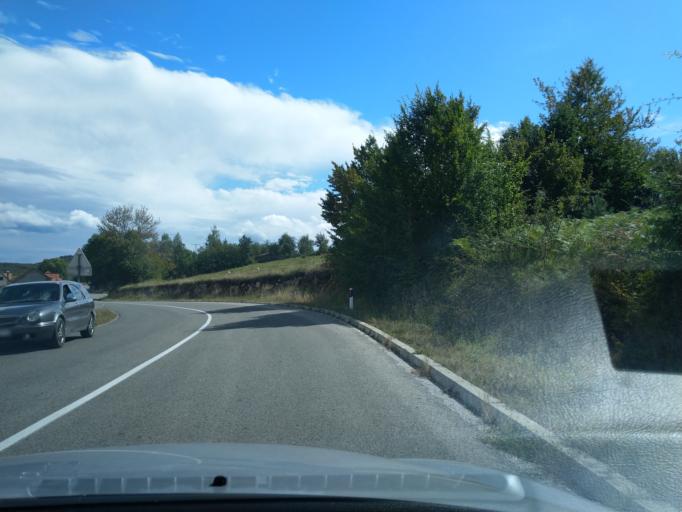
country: RS
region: Central Serbia
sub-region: Zlatiborski Okrug
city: Cajetina
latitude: 43.7215
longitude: 19.8299
